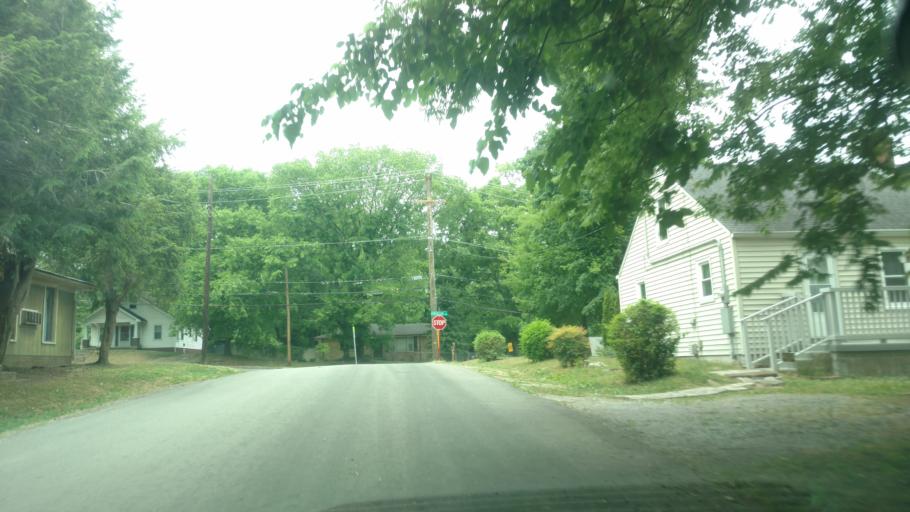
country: US
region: Tennessee
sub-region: Davidson County
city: Nashville
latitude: 36.2026
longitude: -86.7221
